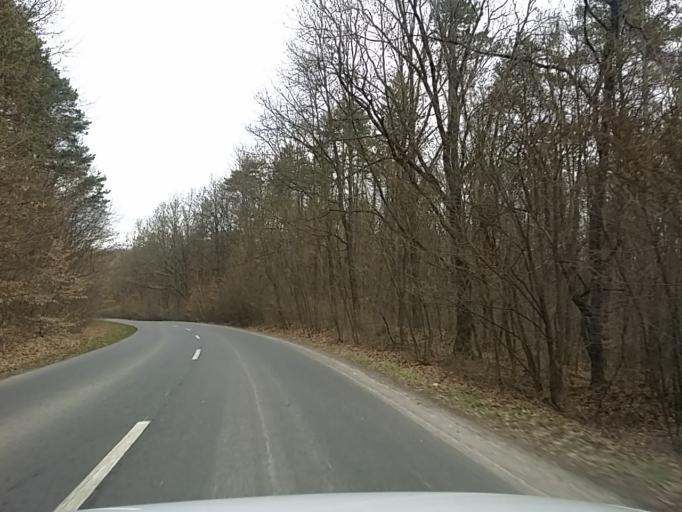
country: HU
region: Borsod-Abauj-Zemplen
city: Putnok
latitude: 48.4501
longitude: 20.4804
